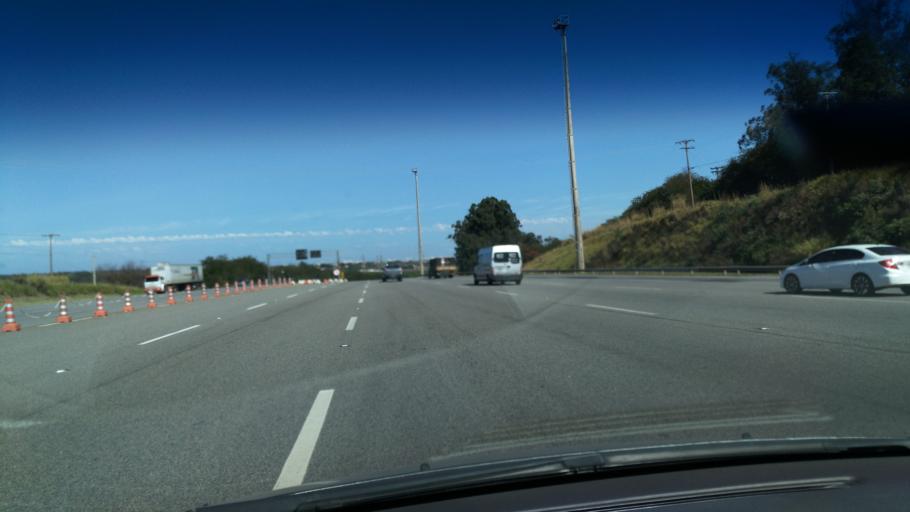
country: BR
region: Sao Paulo
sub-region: Jaguariuna
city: Jaguariuna
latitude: -22.7725
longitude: -47.0223
